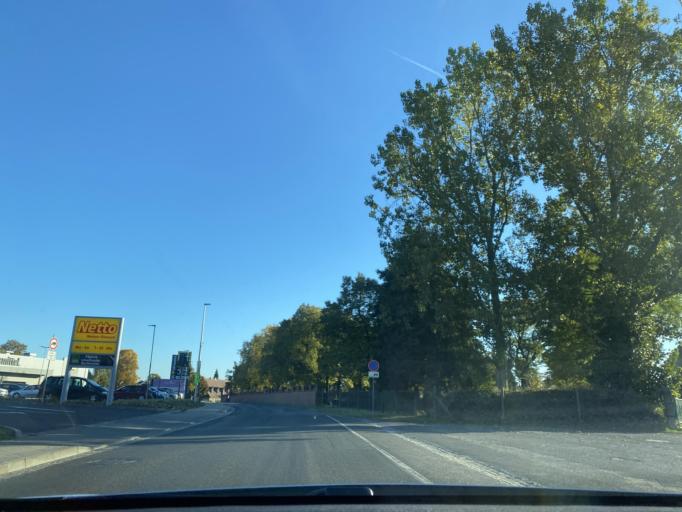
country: DE
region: Saxony
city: Rothenburg
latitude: 51.3305
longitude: 14.9667
